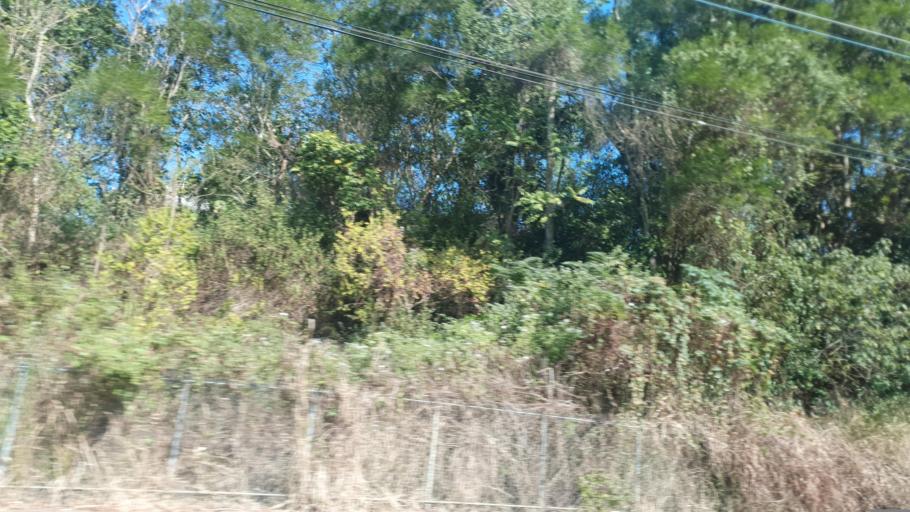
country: TW
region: Taiwan
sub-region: Tainan
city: Tainan
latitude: 23.0368
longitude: 120.3409
